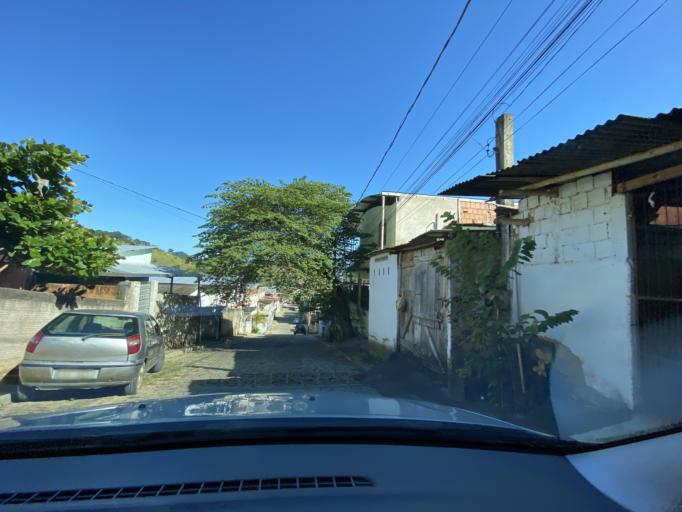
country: BR
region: Espirito Santo
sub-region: Jeronimo Monteiro
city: Jeronimo Monteiro
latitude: -20.7983
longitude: -41.4004
